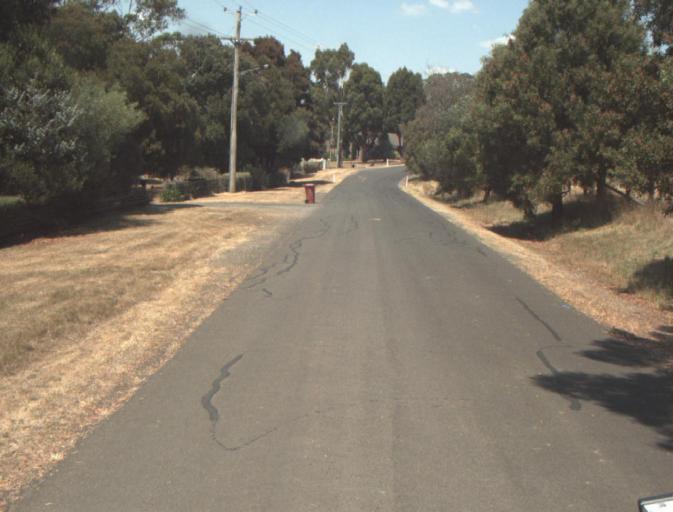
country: AU
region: Tasmania
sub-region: Launceston
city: Newstead
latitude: -41.4885
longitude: 147.1839
